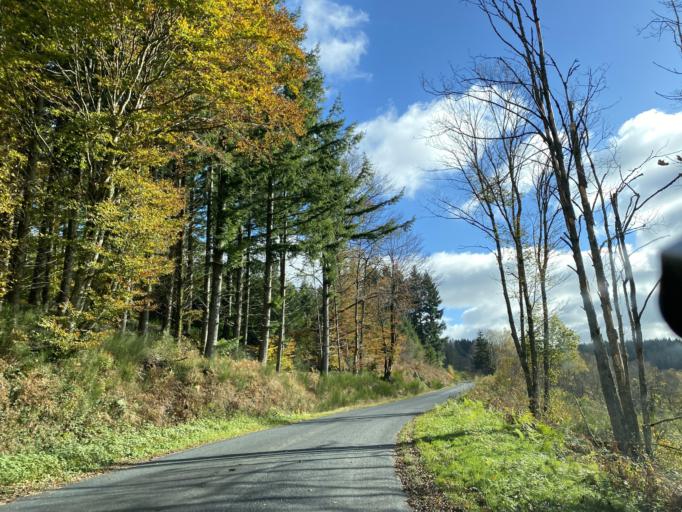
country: FR
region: Auvergne
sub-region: Departement du Puy-de-Dome
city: Celles-sur-Durolle
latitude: 45.7912
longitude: 3.6596
